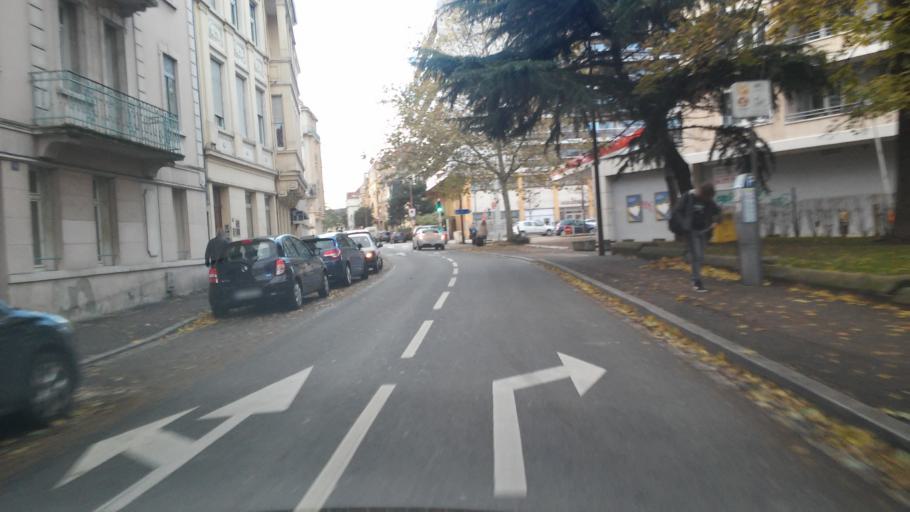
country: FR
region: Lorraine
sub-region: Departement de la Moselle
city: Metz
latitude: 49.1092
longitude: 6.1713
